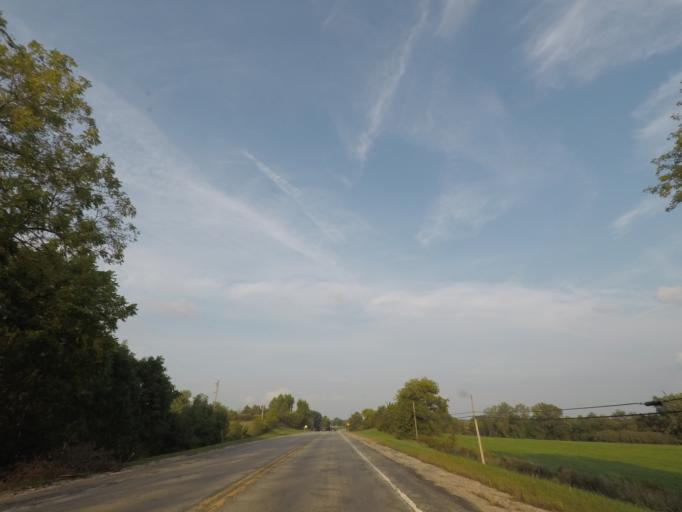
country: US
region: Wisconsin
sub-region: Dane County
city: Cottage Grove
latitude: 43.0866
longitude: -89.2512
